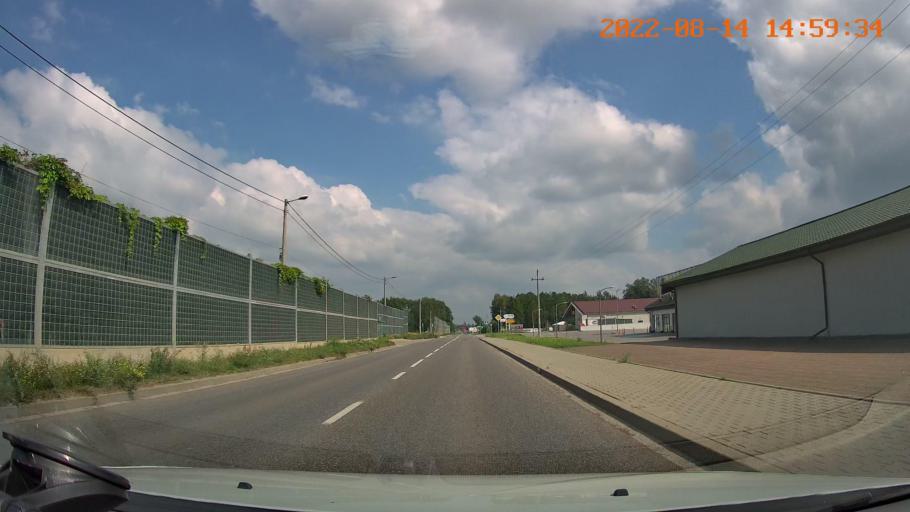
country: PL
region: Swietokrzyskie
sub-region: Powiat kielecki
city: Piekoszow
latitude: 50.8811
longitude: 20.4842
